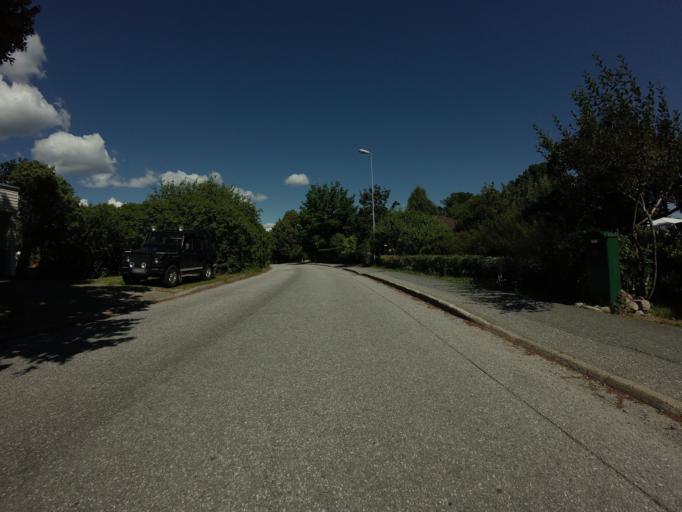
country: SE
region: Stockholm
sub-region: Sollentuna Kommun
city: Sollentuna
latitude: 59.4534
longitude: 17.9023
